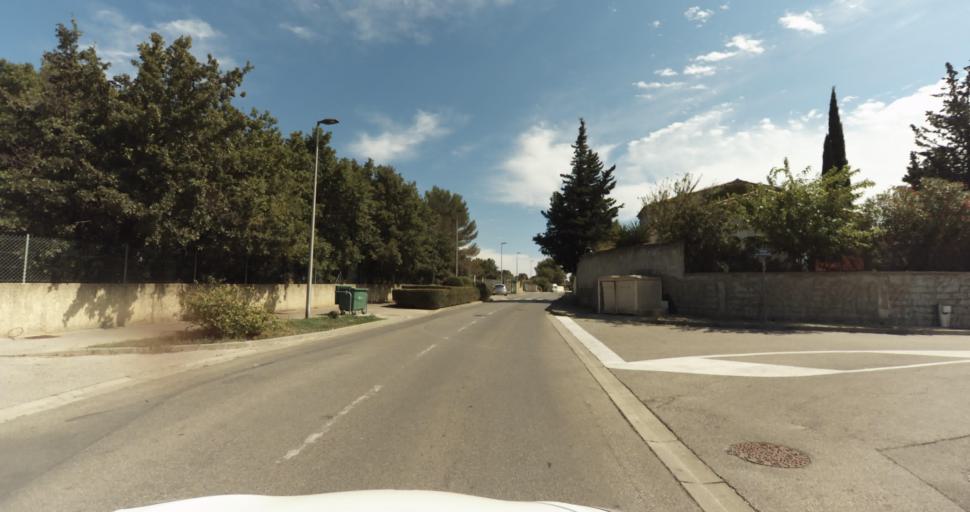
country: FR
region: Provence-Alpes-Cote d'Azur
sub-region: Departement des Bouches-du-Rhone
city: Miramas
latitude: 43.5828
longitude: 5.0183
